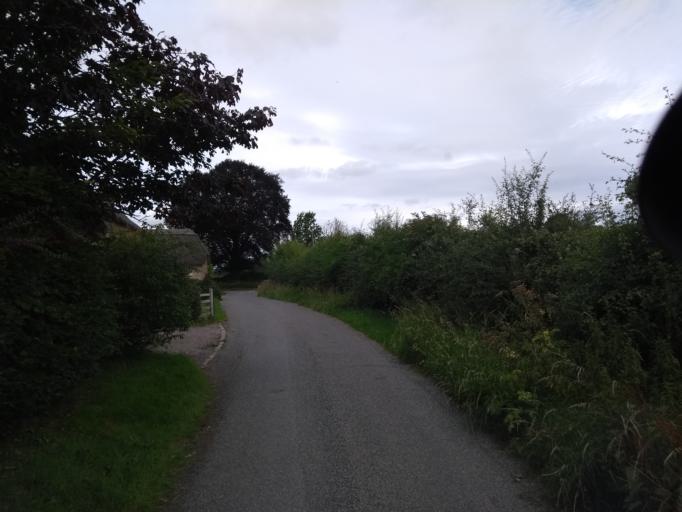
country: GB
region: England
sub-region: Somerset
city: Ilminster
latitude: 50.9377
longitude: -2.8841
